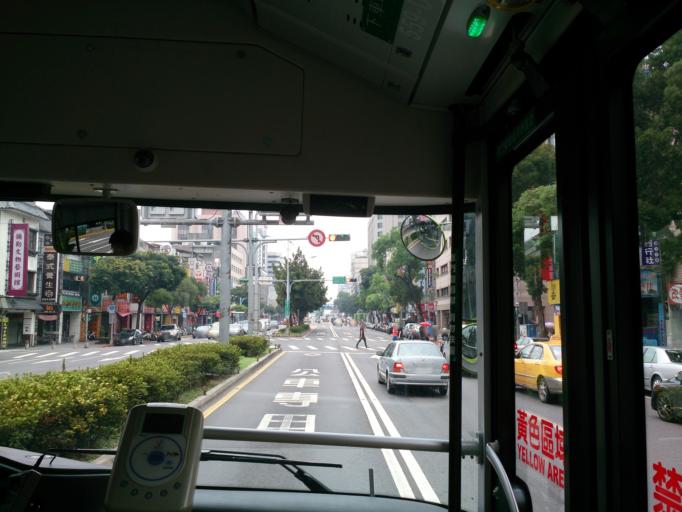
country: TW
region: Taipei
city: Taipei
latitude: 25.0625
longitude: 121.5324
